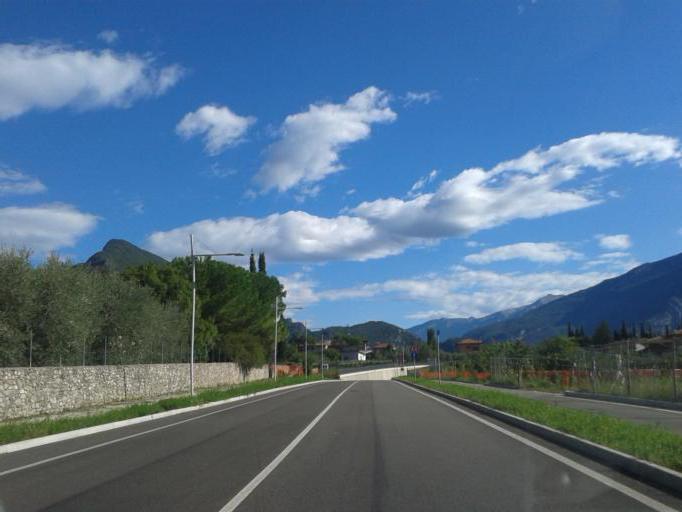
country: IT
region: Trentino-Alto Adige
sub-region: Provincia di Trento
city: Riva del Garda
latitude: 45.9014
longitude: 10.8408
